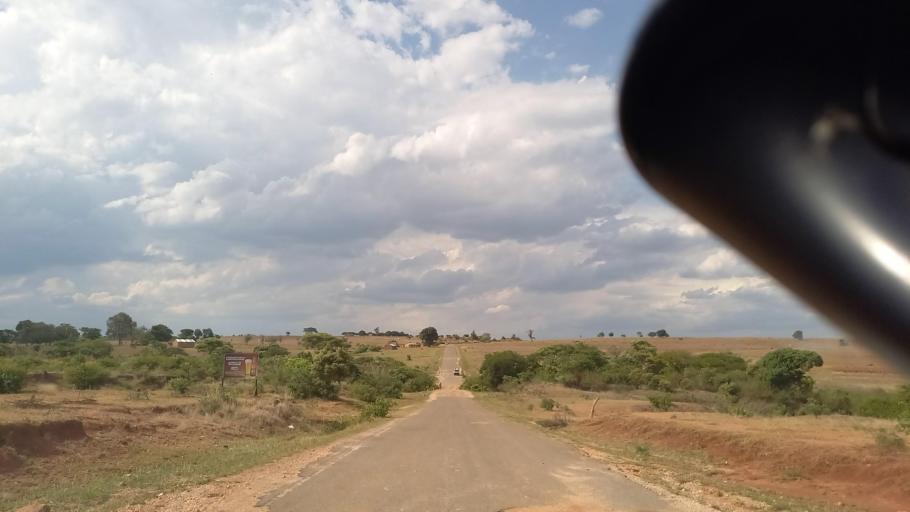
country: ZM
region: Lusaka
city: Kafue
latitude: -16.2106
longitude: 28.1117
